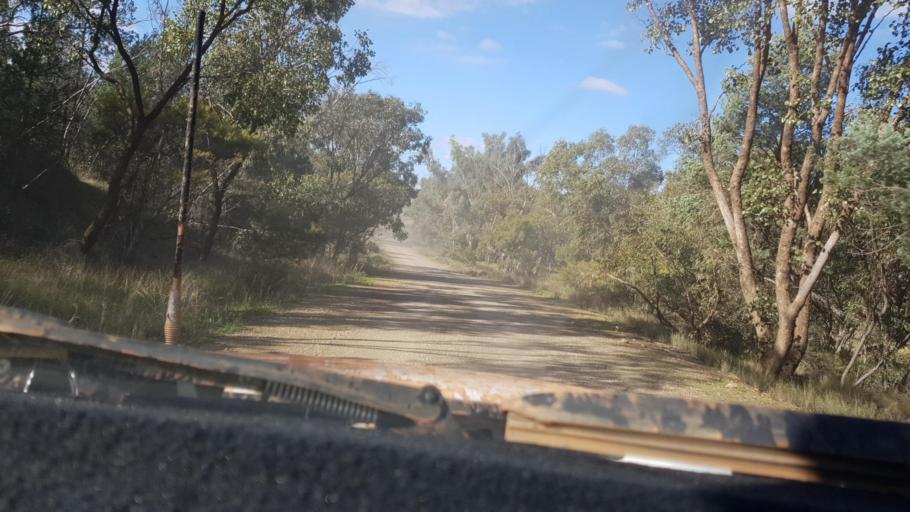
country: AU
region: New South Wales
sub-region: Lachlan
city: Condobolin
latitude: -33.1397
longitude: 147.3109
